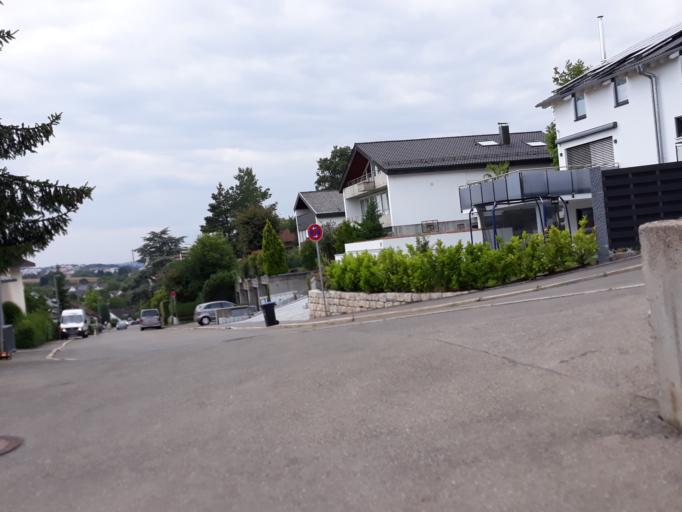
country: DE
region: Baden-Wuerttemberg
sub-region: Regierungsbezirk Stuttgart
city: Boeblingen
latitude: 48.6762
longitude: 9.0377
